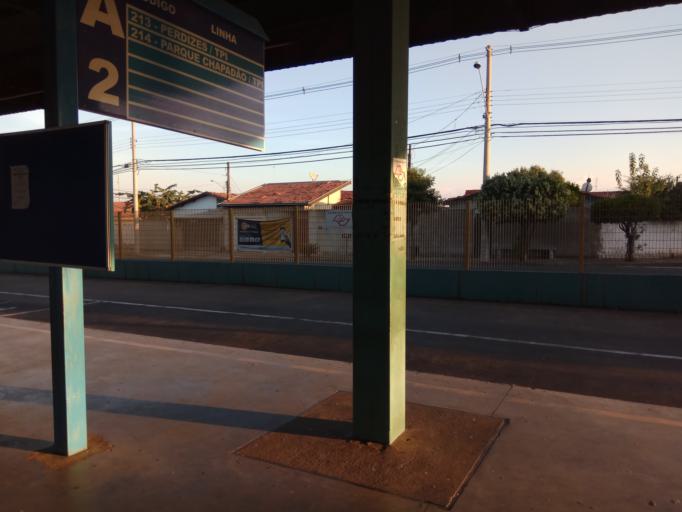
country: BR
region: Sao Paulo
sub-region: Rio Das Pedras
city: Rio das Pedras
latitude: -22.7730
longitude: -47.5960
